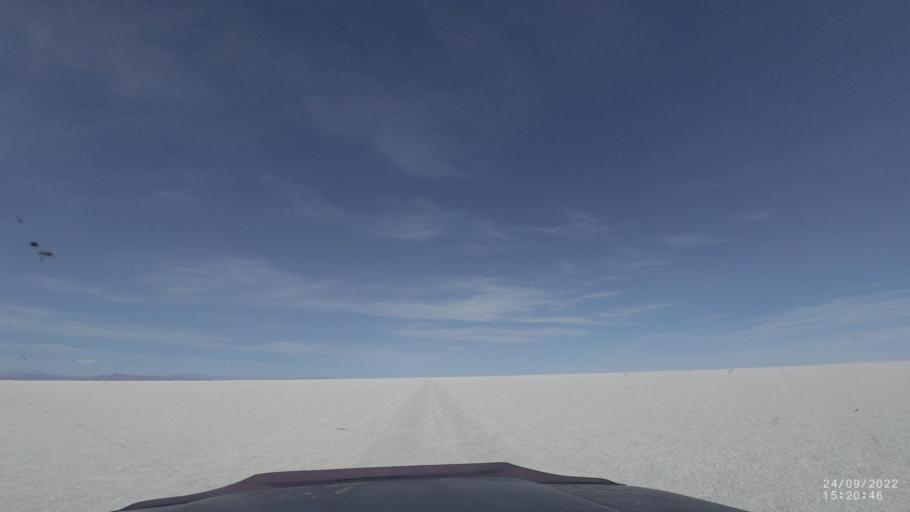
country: BO
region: Potosi
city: Colchani
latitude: -20.0151
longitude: -67.3957
